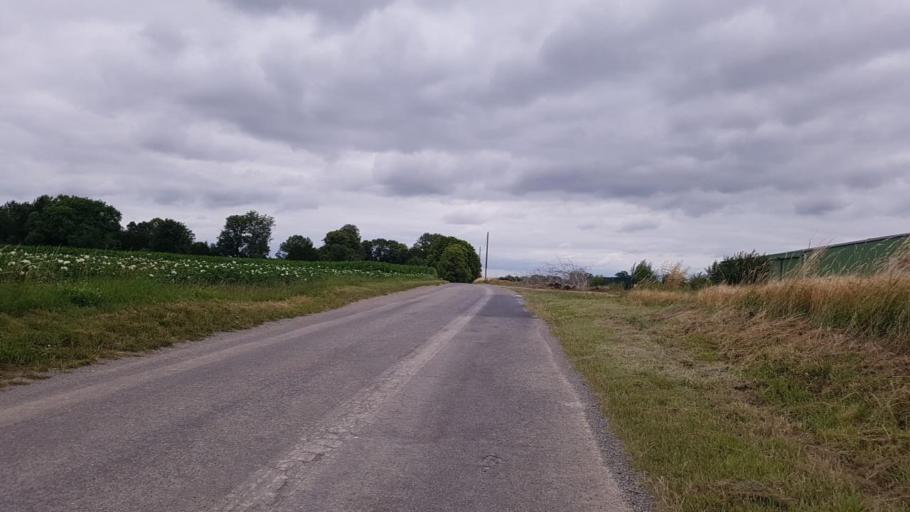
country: FR
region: Picardie
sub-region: Departement de l'Aisne
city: Guise
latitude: 49.8946
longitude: 3.6106
